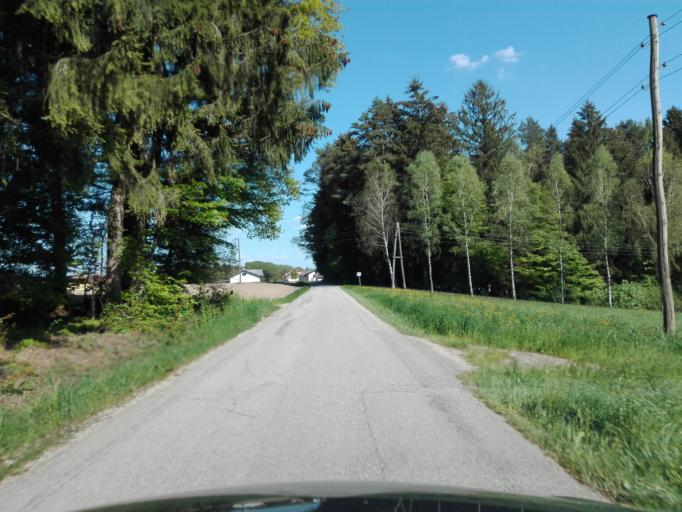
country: AT
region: Upper Austria
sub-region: Politischer Bezirk Rohrbach
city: Pfarrkirchen im Muehlkreis
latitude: 48.4240
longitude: 13.7255
